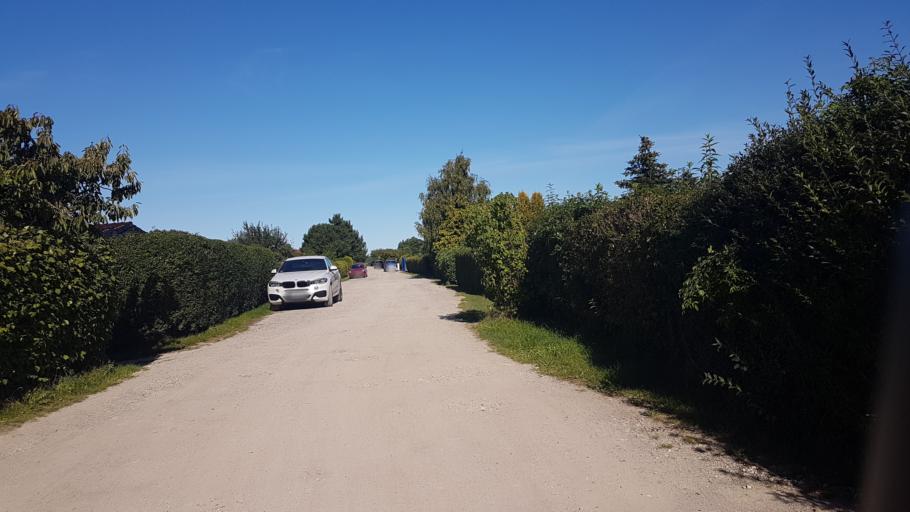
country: DE
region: Mecklenburg-Vorpommern
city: Glowe
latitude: 54.5447
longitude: 13.5069
